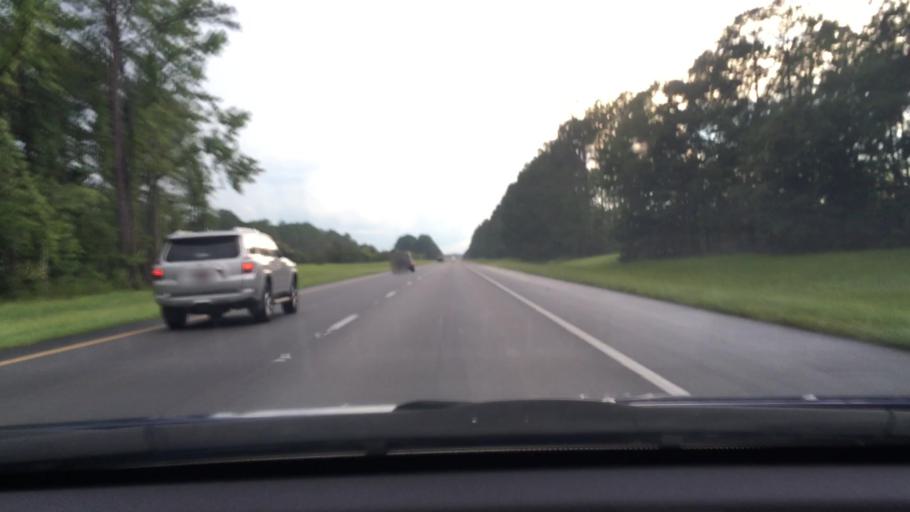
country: US
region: South Carolina
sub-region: Lee County
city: Bishopville
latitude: 34.1959
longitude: -80.3041
